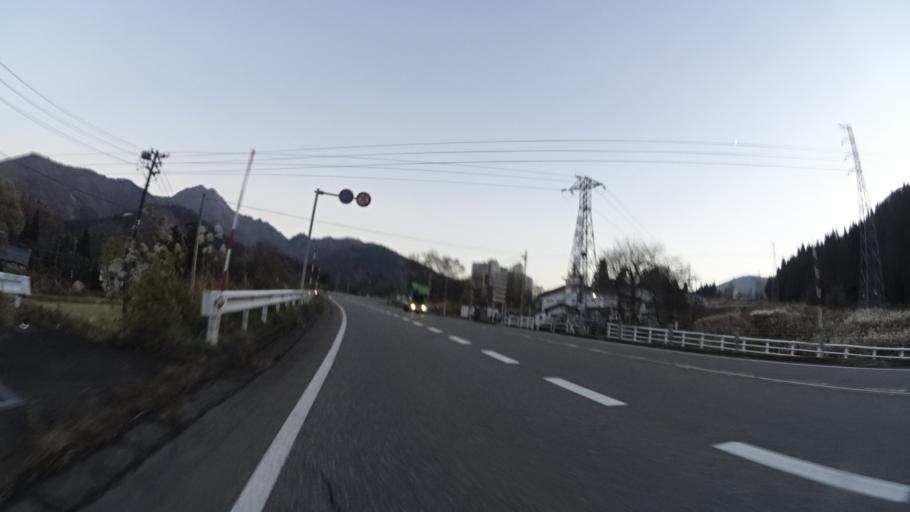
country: JP
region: Niigata
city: Shiozawa
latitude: 36.9724
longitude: 138.8005
